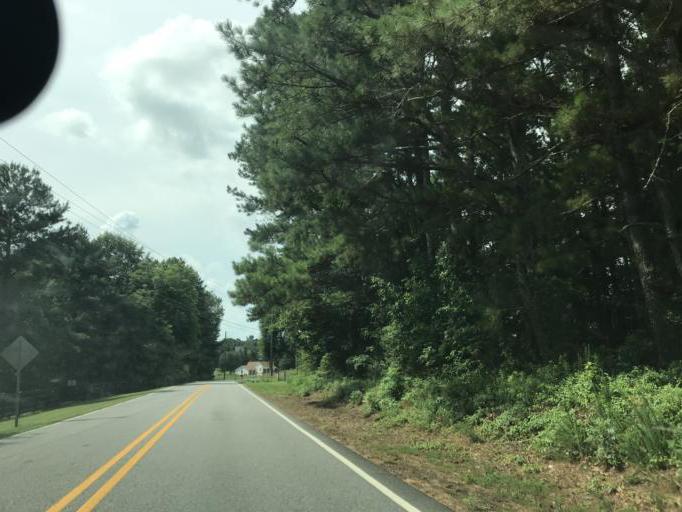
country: US
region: Georgia
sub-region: Forsyth County
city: Cumming
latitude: 34.2246
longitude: -84.2420
